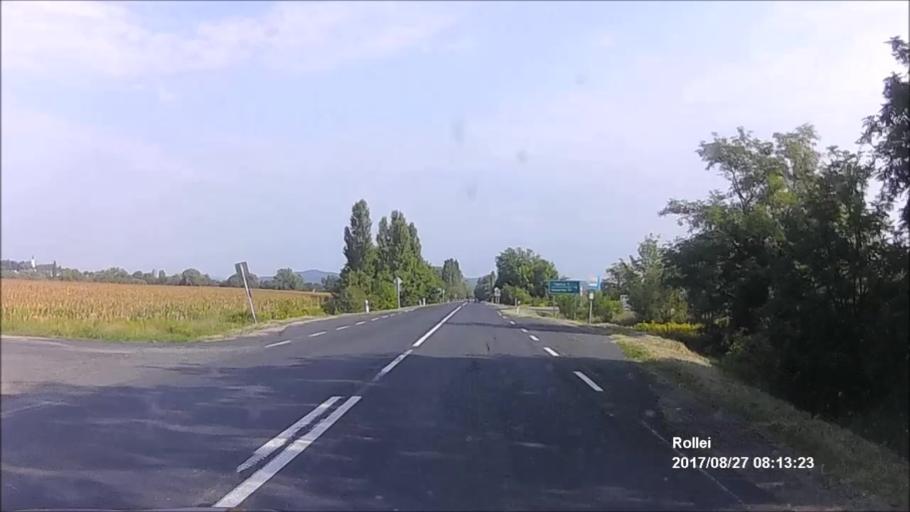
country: HU
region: Veszprem
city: Tapolca
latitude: 46.8442
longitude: 17.3711
